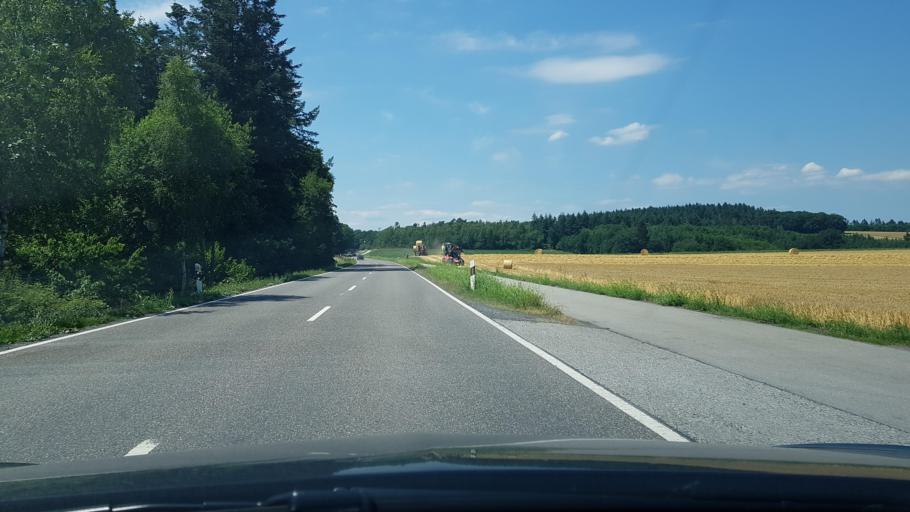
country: DE
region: Rheinland-Pfalz
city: Ediger-Eller
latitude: 50.1315
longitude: 7.1466
